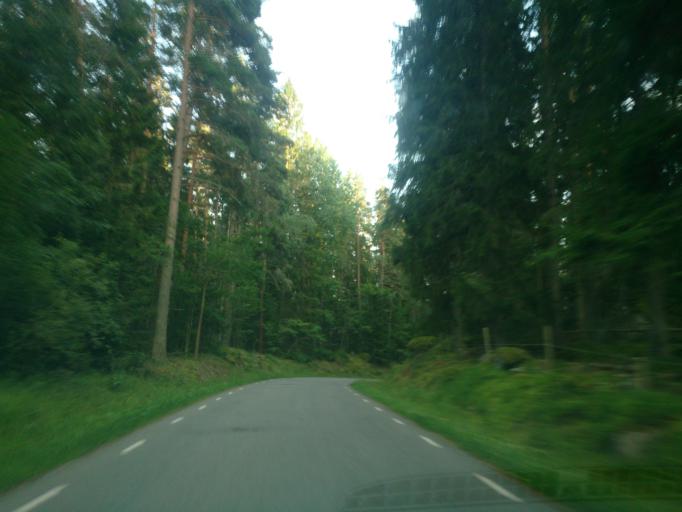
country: SE
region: OEstergoetland
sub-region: Atvidabergs Kommun
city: Atvidaberg
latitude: 58.2872
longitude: 16.0955
